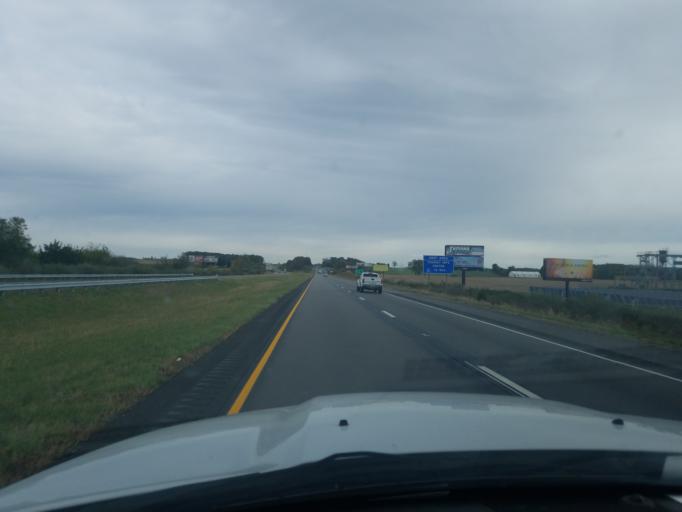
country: US
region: Indiana
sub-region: Spencer County
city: Dale
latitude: 38.1942
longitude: -86.9670
